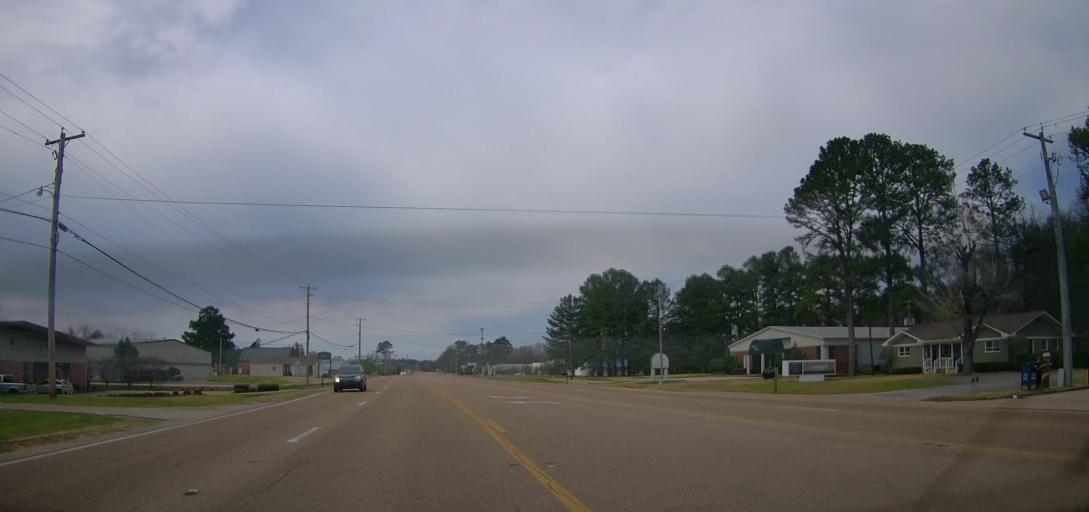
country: US
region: Mississippi
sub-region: Lee County
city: Tupelo
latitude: 34.2855
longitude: -88.7389
